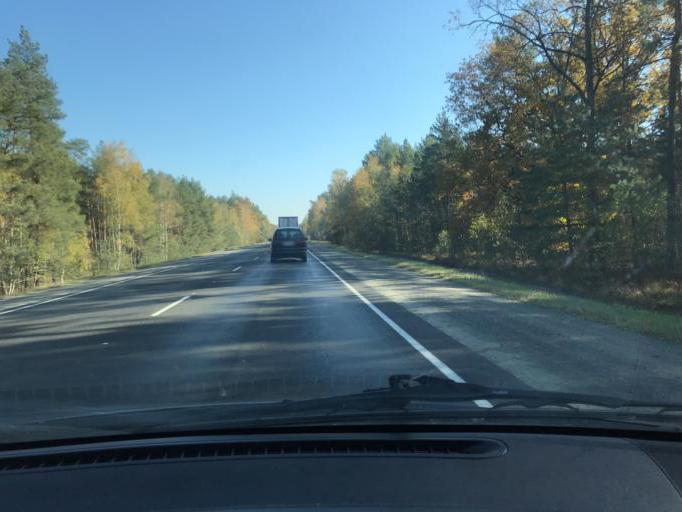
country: BY
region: Brest
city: Mikashevichy
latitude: 52.2450
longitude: 27.4231
